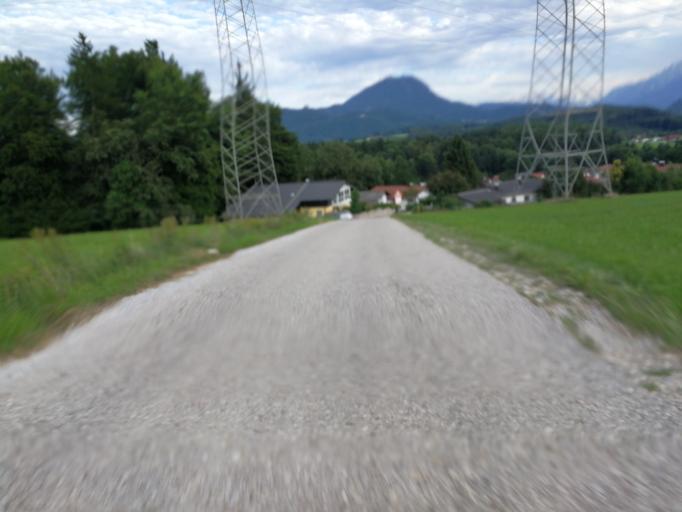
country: AT
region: Salzburg
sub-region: Politischer Bezirk Salzburg-Umgebung
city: Elixhausen
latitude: 47.8672
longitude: 13.0529
